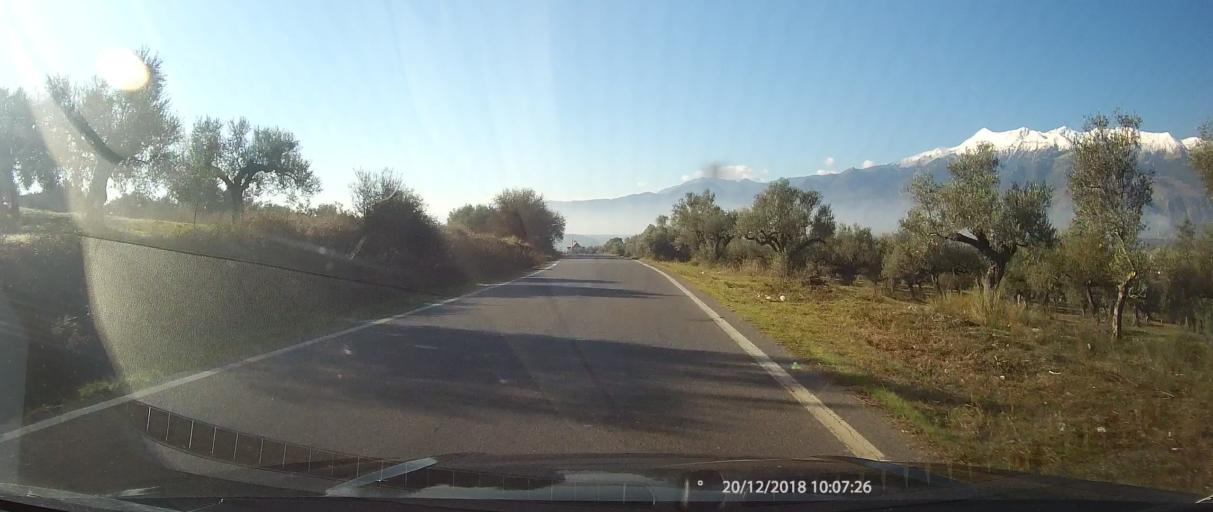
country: GR
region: Peloponnese
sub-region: Nomos Lakonias
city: Sparti
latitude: 37.0191
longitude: 22.4955
